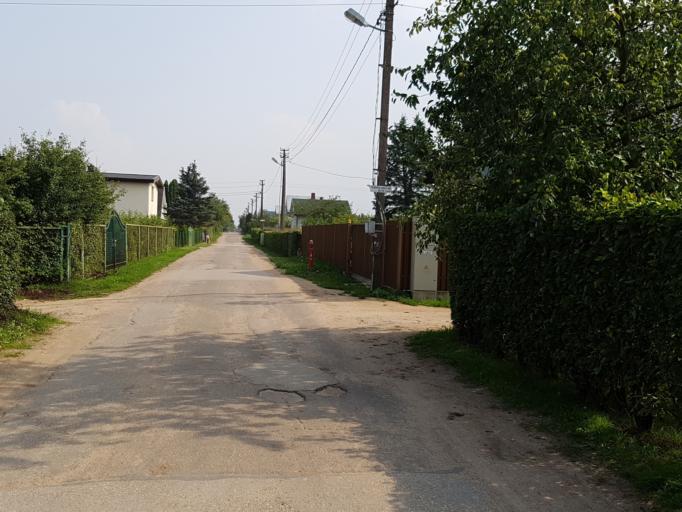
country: LT
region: Vilnius County
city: Rasos
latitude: 54.7935
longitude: 25.3634
